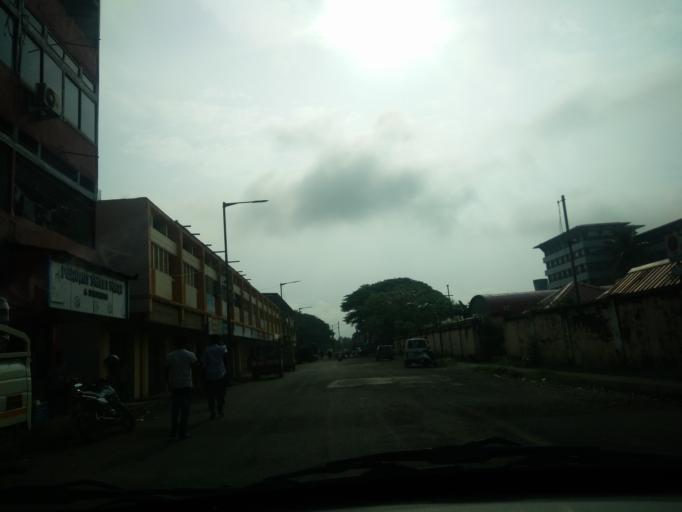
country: IN
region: Goa
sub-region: South Goa
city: Madgaon
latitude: 15.2679
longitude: 73.9640
